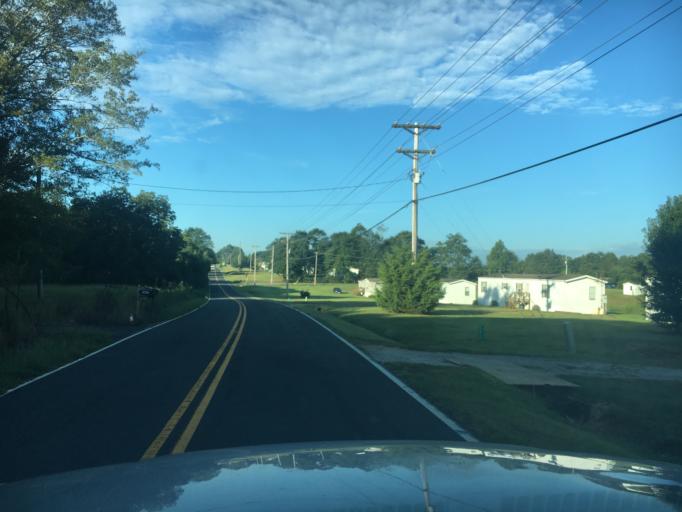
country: US
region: South Carolina
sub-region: Spartanburg County
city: Woodruff
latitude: 34.6336
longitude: -82.0571
